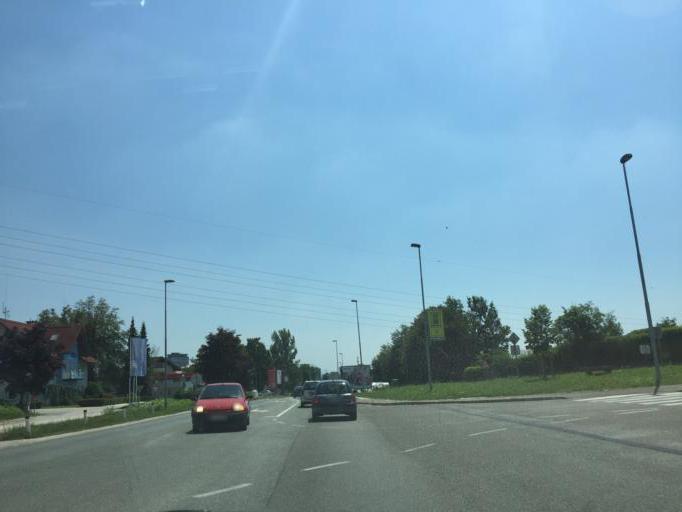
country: SI
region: Kranj
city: Kranj
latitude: 46.2501
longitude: 14.3464
